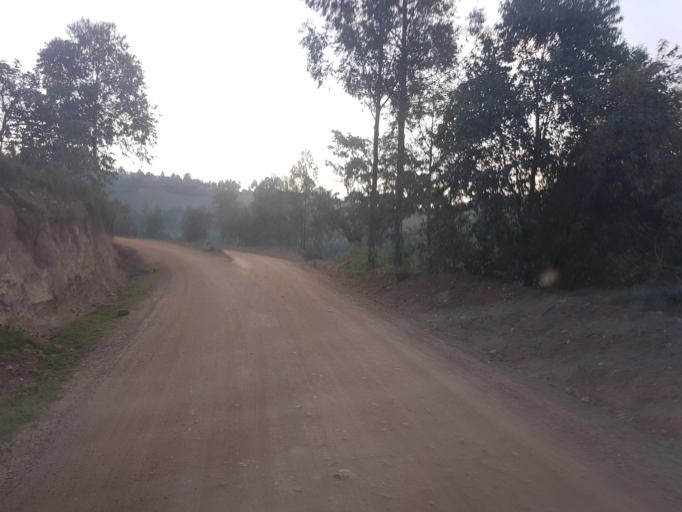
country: UG
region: Western Region
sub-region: Rukungiri District
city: Rukungiri
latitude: -0.7504
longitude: 29.9299
